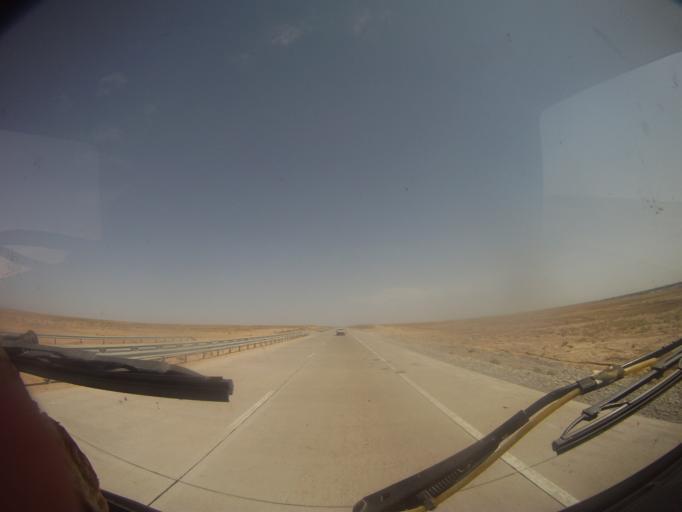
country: KZ
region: Ongtustik Qazaqstan
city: Temirlanovka
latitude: 42.5169
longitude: 69.4220
